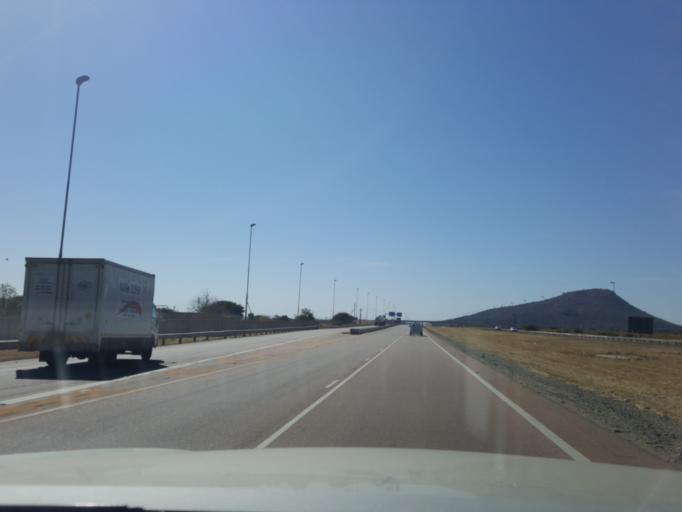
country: ZA
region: North-West
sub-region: Bojanala Platinum District Municipality
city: Brits
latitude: -25.7236
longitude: 27.6769
